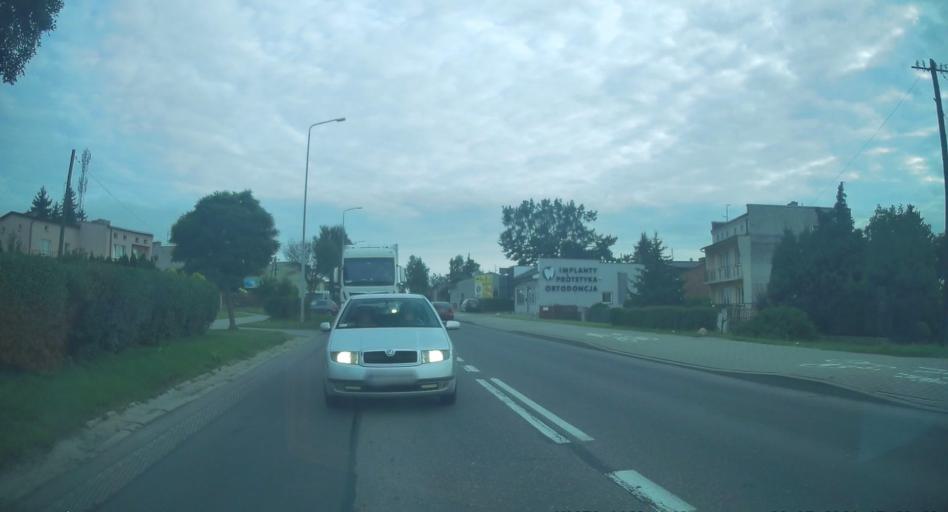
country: PL
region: Lodz Voivodeship
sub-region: Powiat radomszczanski
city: Radomsko
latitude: 51.0578
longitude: 19.4410
